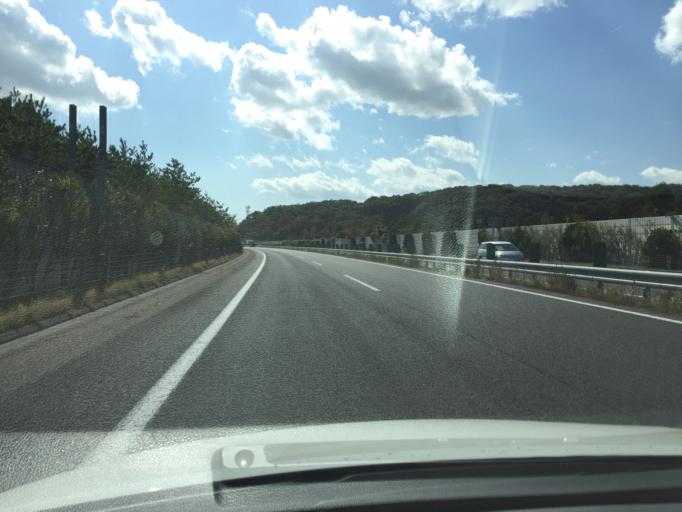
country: JP
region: Fukushima
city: Koriyama
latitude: 37.3988
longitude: 140.3109
